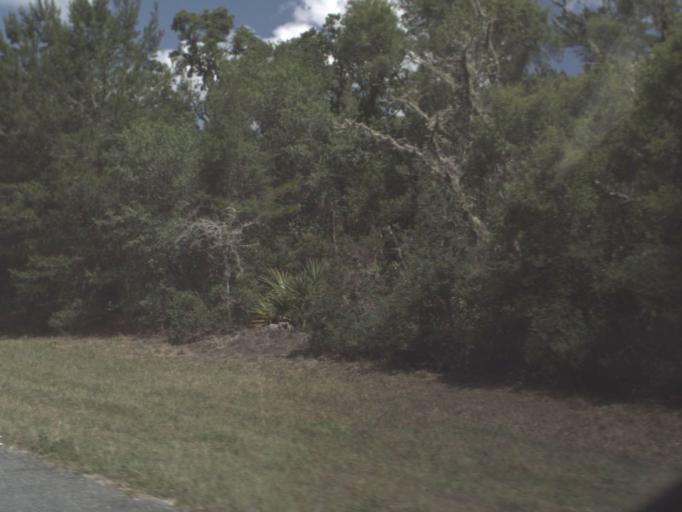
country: US
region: Florida
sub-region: Lake County
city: Astor
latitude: 29.1774
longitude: -81.7041
